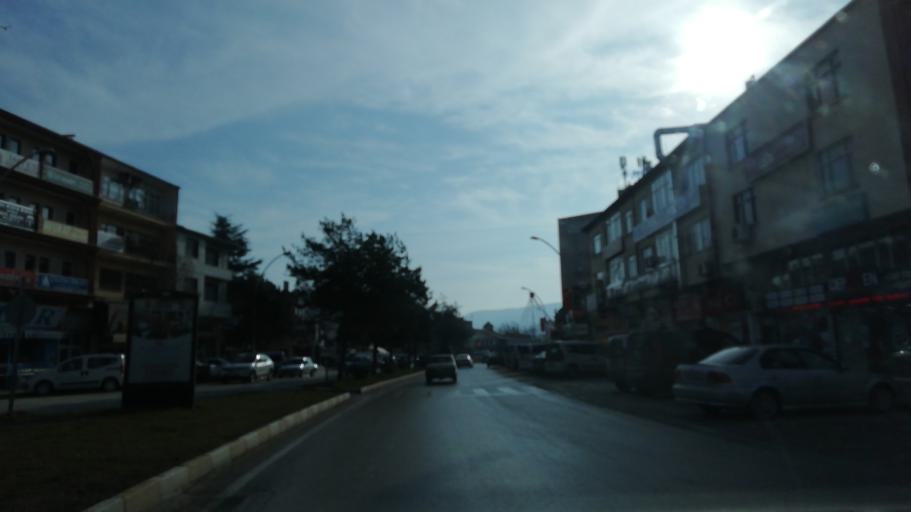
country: TR
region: Karabuk
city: Safranbolu
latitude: 41.2504
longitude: 32.6820
